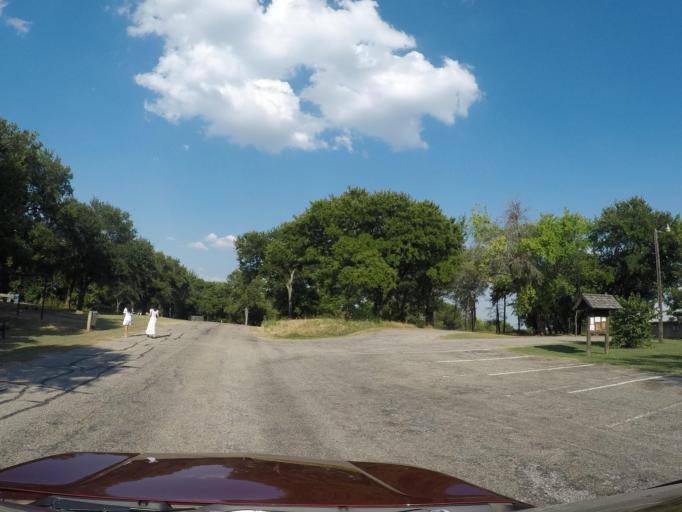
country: US
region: Texas
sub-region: Grayson County
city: Preston
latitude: 33.8229
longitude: -96.6110
